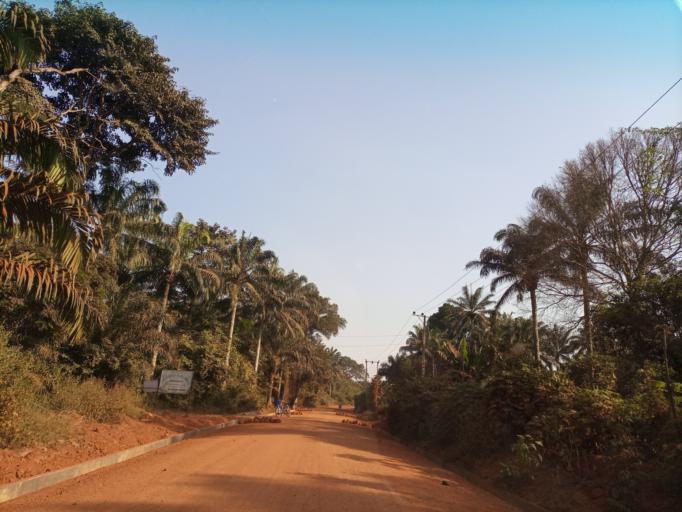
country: NG
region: Enugu
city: Opi
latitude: 6.7539
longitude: 7.4065
